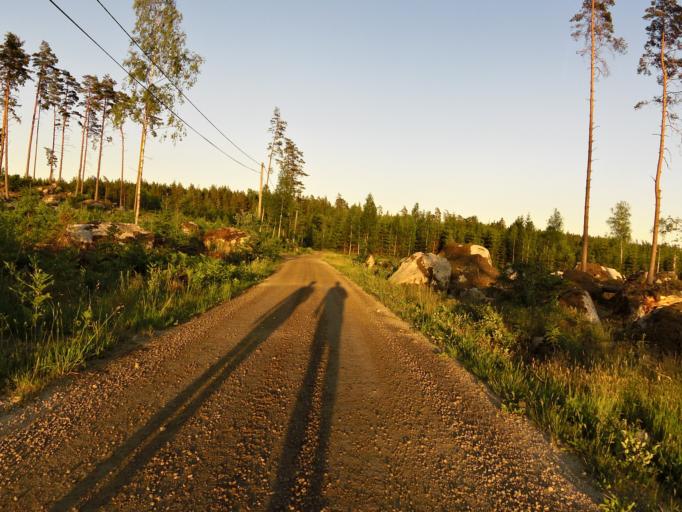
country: SE
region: Blekinge
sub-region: Olofstroms Kommun
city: Olofstroem
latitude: 56.4122
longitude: 14.5456
